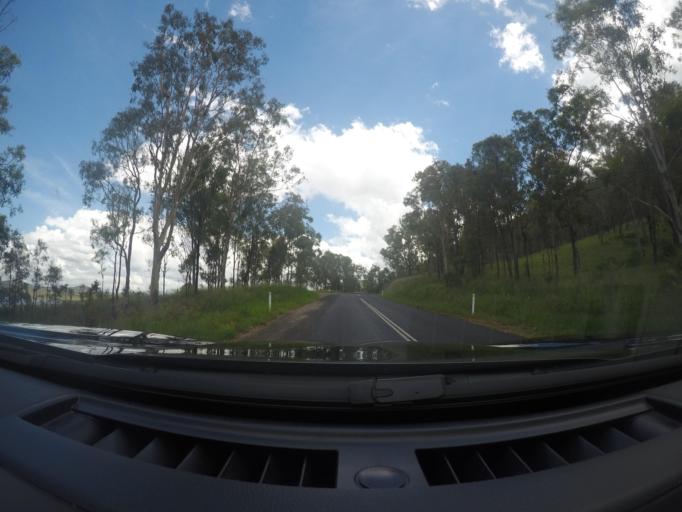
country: AU
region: Queensland
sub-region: Moreton Bay
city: Woodford
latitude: -27.0902
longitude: 152.5629
